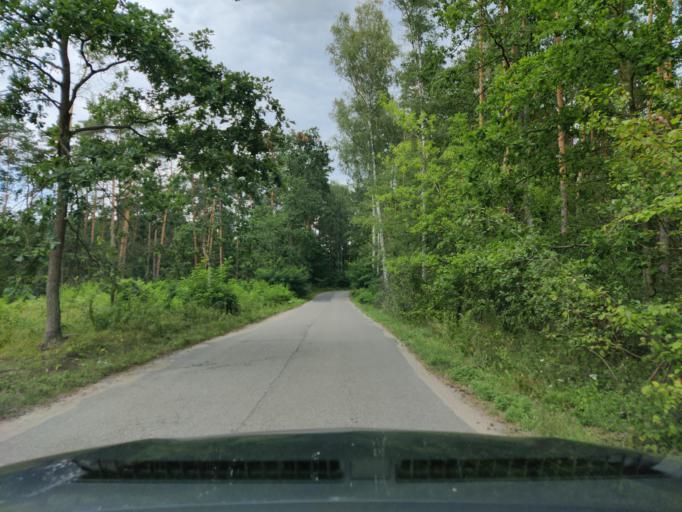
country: PL
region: Masovian Voivodeship
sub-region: Powiat pultuski
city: Pultusk
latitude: 52.7343
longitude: 21.1371
